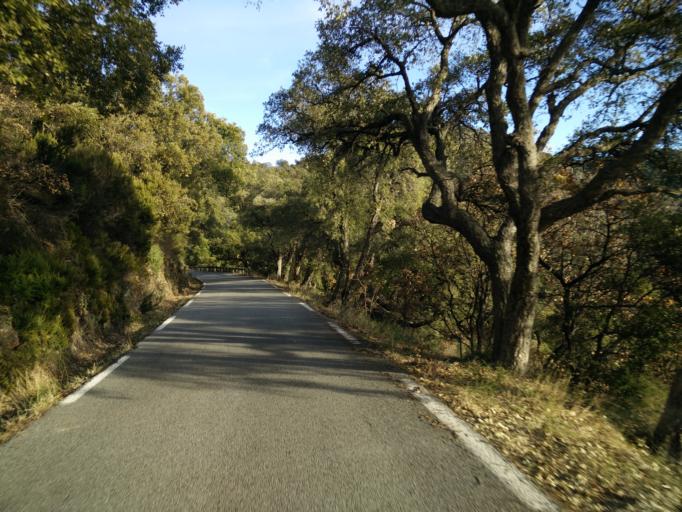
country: FR
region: Provence-Alpes-Cote d'Azur
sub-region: Departement du Var
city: Collobrieres
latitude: 43.2029
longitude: 6.3076
